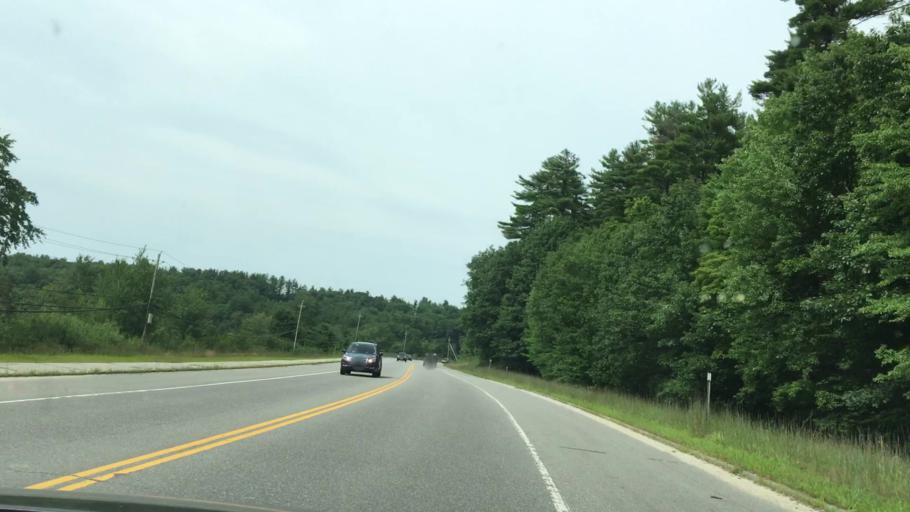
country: US
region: New Hampshire
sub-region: Hillsborough County
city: Peterborough
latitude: 42.8941
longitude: -71.9429
